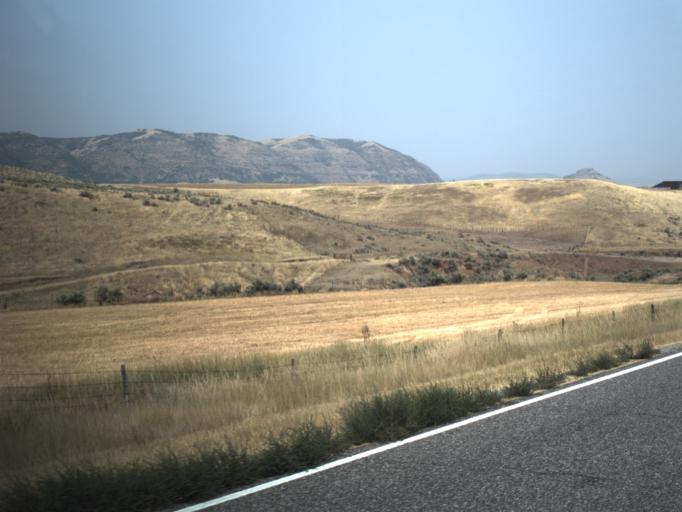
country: US
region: Utah
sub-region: Summit County
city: Coalville
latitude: 41.0094
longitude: -111.5170
